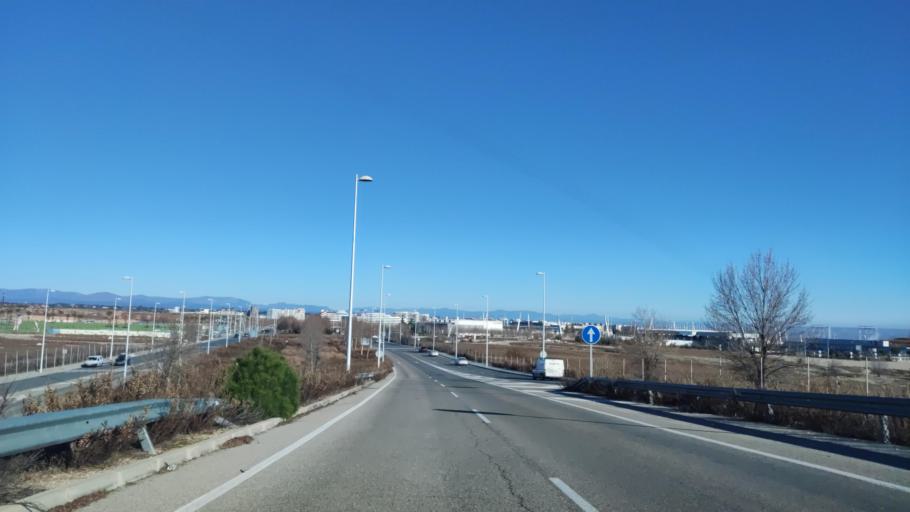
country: ES
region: Madrid
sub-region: Provincia de Madrid
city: Hortaleza
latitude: 40.4730
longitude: -3.6182
